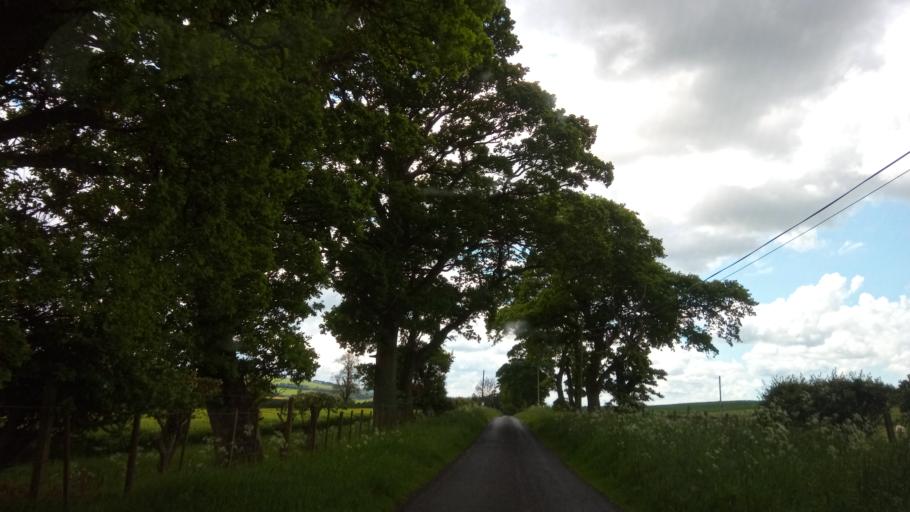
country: GB
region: Scotland
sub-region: The Scottish Borders
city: Coldstream
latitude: 55.5776
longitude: -2.3182
